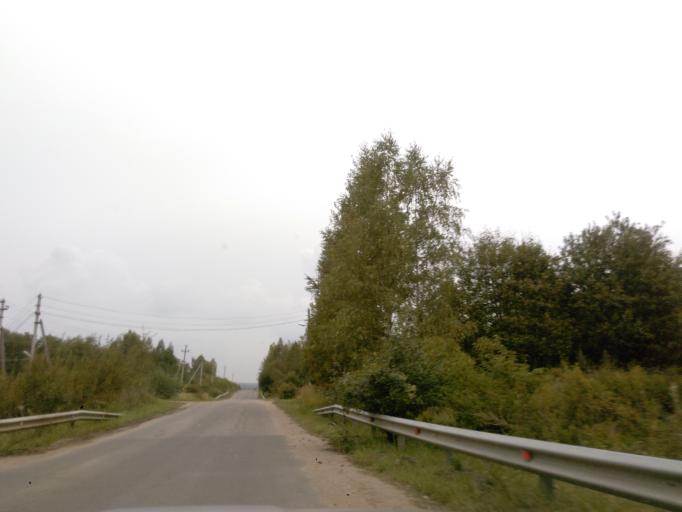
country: RU
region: Moskovskaya
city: Mendeleyevo
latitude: 56.1062
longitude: 37.2526
